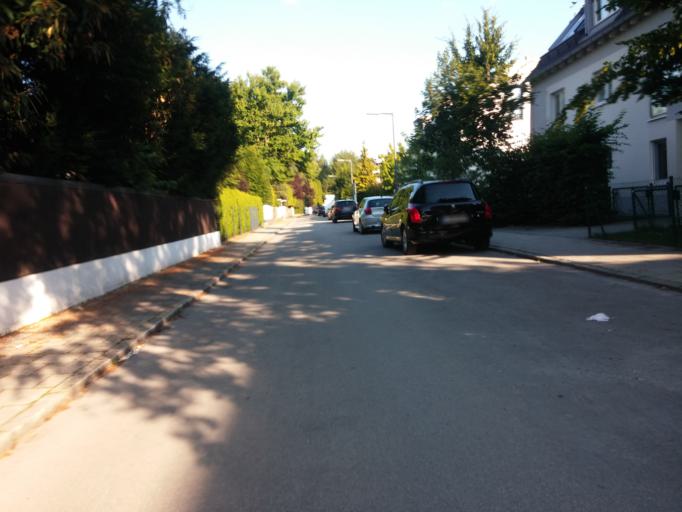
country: DE
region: Bavaria
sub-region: Upper Bavaria
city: Neubiberg
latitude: 48.1063
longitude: 11.6722
